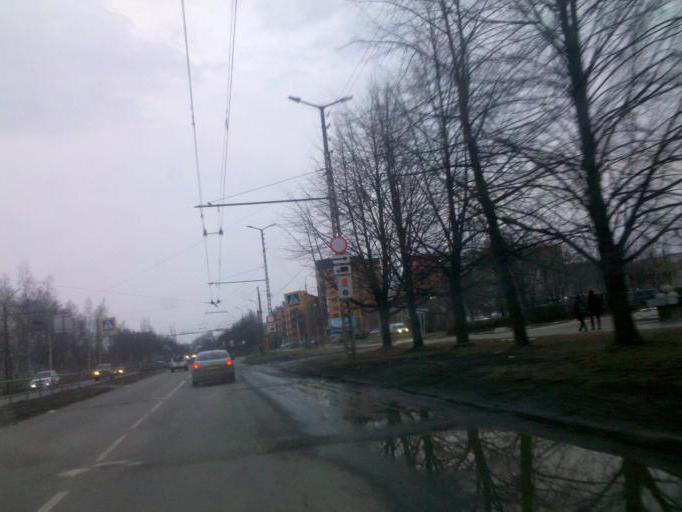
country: RU
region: Republic of Karelia
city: Petrozavodsk
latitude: 61.8041
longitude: 34.3477
